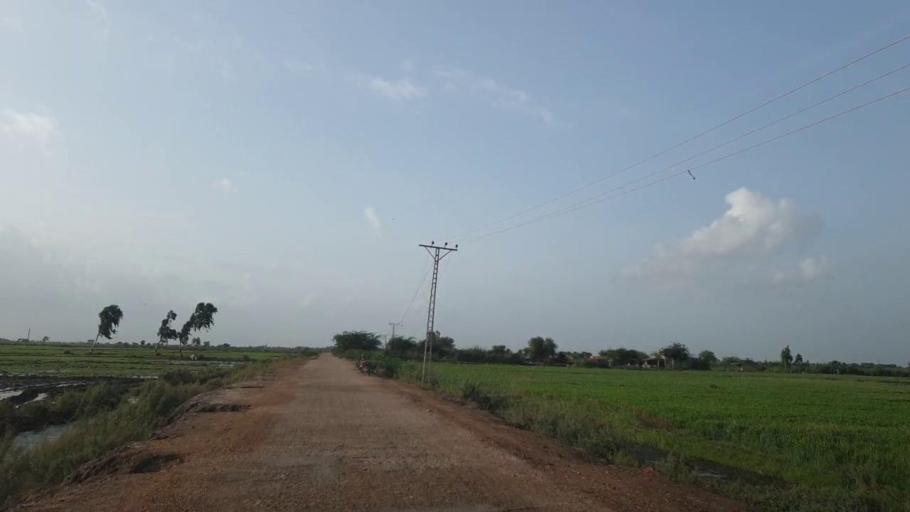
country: PK
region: Sindh
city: Tando Bago
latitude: 24.6583
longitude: 69.1119
